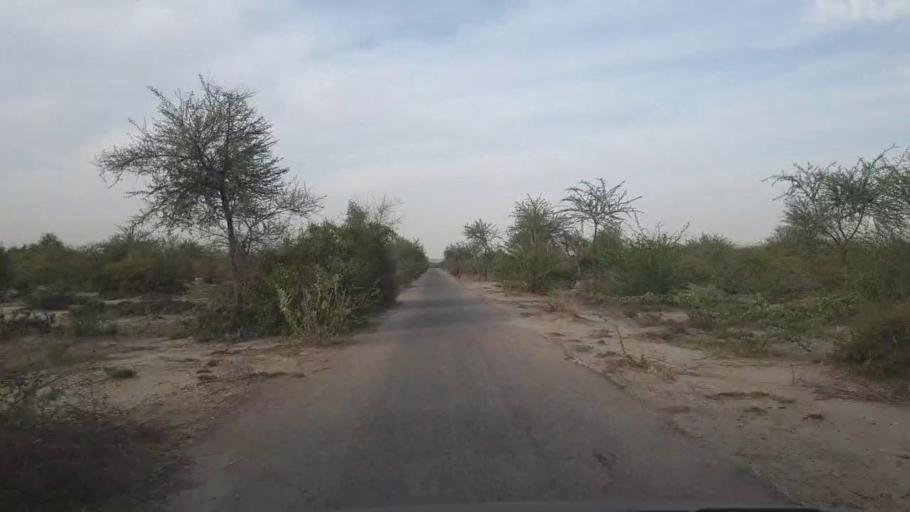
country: PK
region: Sindh
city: Nabisar
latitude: 25.1090
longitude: 69.6772
